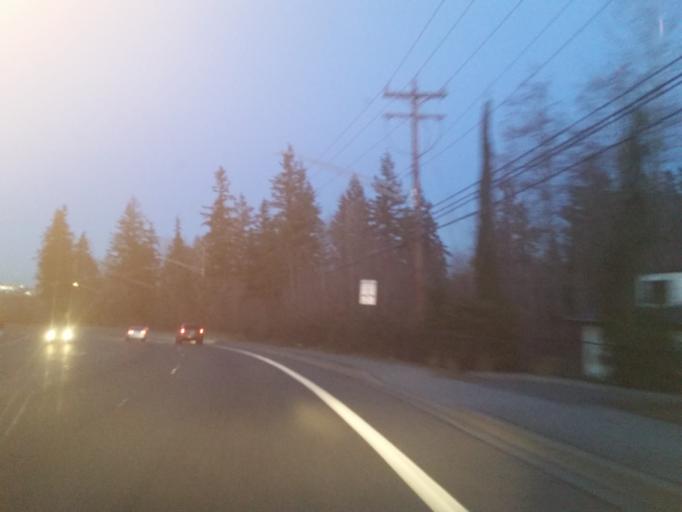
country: US
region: Washington
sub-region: Snohomish County
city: Martha Lake
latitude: 47.8840
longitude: -122.2784
